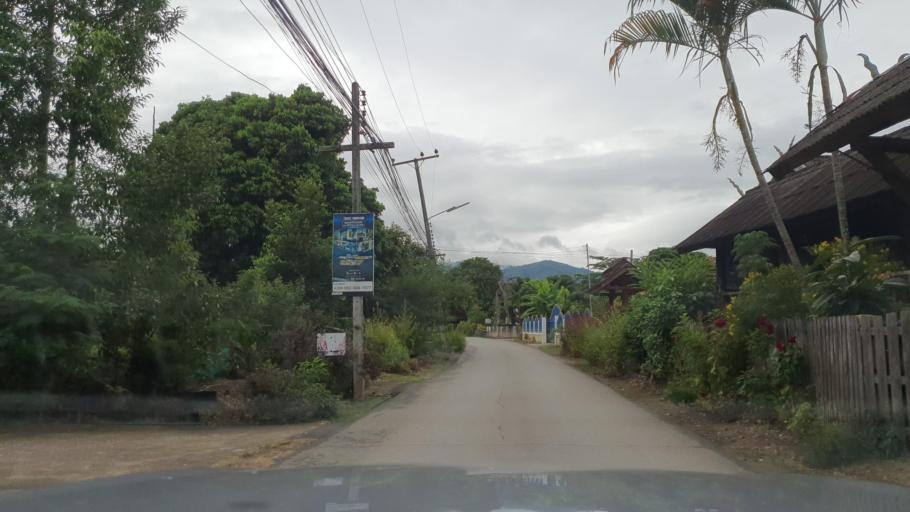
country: TH
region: Chiang Mai
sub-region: Amphoe Chiang Dao
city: Chiang Dao
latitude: 19.3297
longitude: 98.9524
